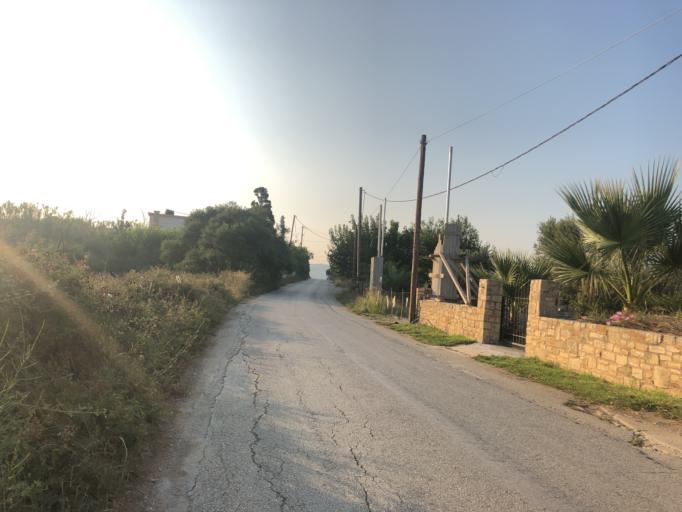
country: GR
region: Crete
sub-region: Nomos Chanias
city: Georgioupolis
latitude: 35.3493
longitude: 24.2836
